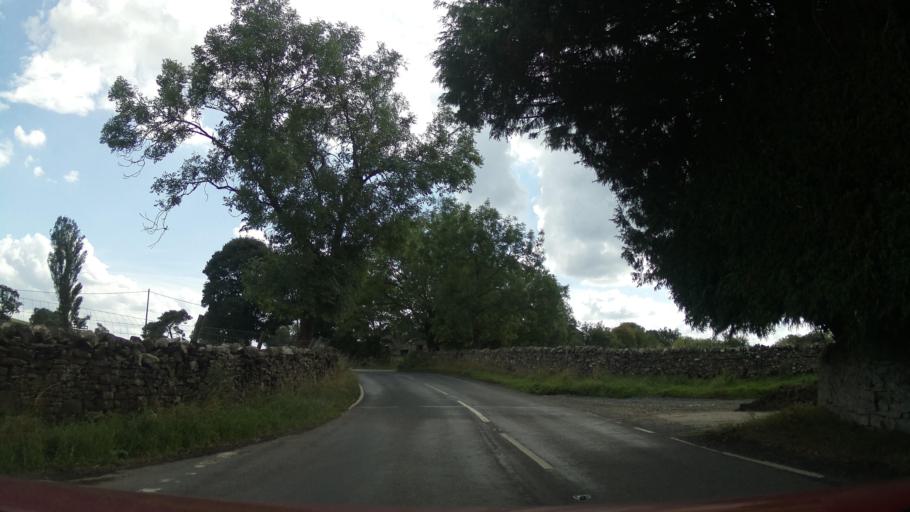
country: GB
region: England
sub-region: North Yorkshire
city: Leyburn
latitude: 54.3761
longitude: -1.8299
